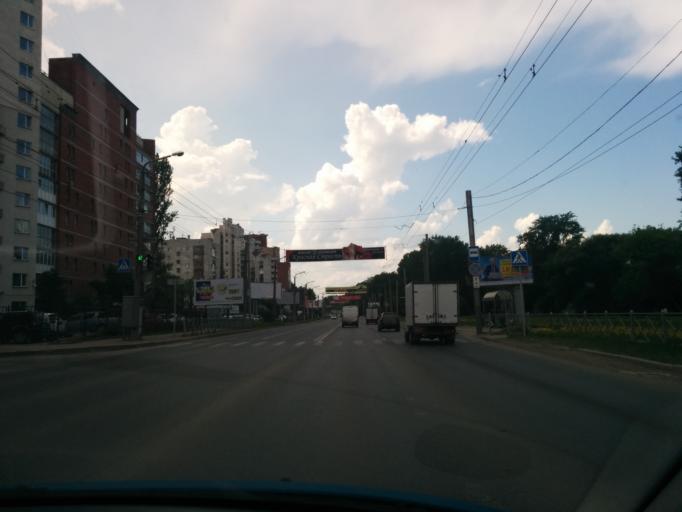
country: RU
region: Perm
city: Kondratovo
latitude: 57.9798
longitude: 56.1741
